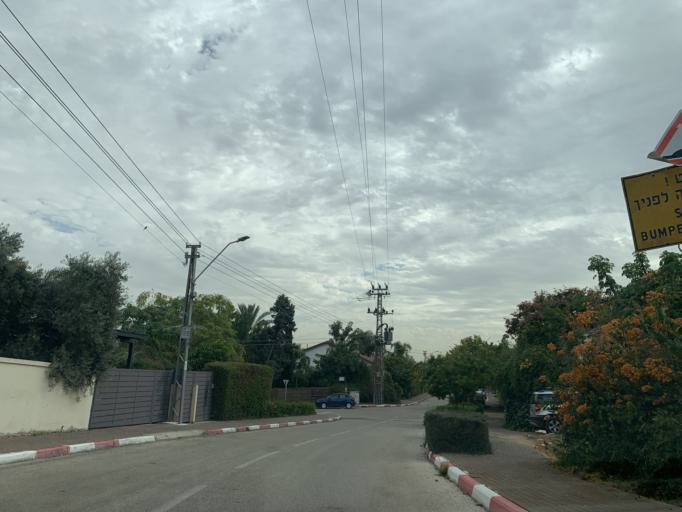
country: IL
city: Nirit
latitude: 32.1454
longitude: 34.9874
